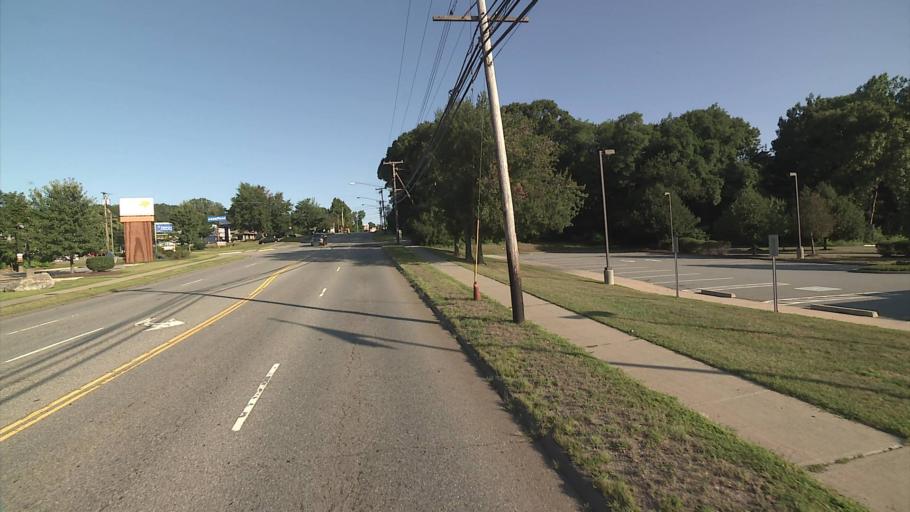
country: US
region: Connecticut
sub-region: New London County
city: Long Hill
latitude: 41.3506
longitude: -72.0565
